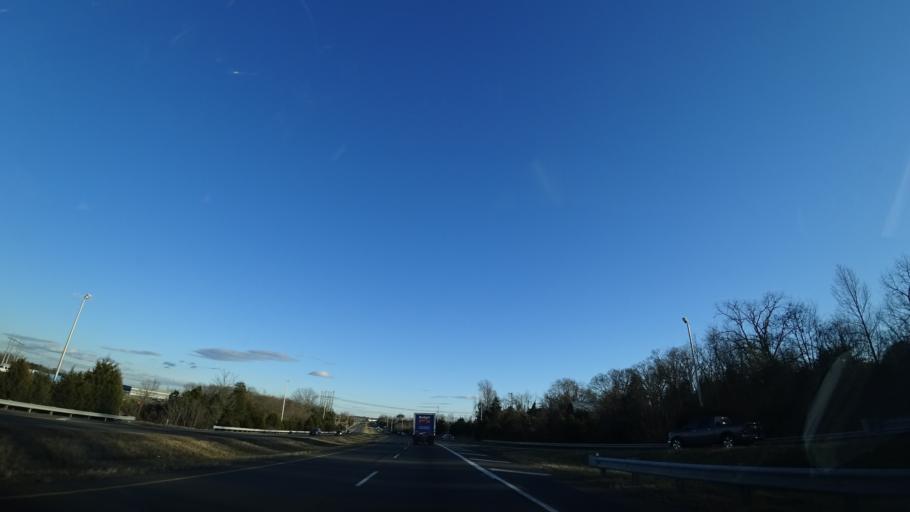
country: US
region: Virginia
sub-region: Prince William County
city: Linton Hall
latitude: 38.7958
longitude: -77.5692
